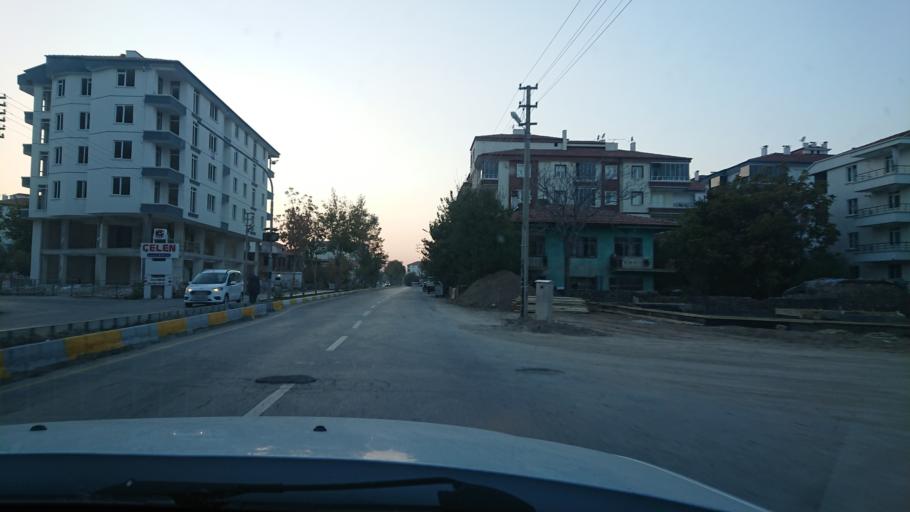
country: TR
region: Aksaray
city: Aksaray
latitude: 38.3604
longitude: 34.0159
